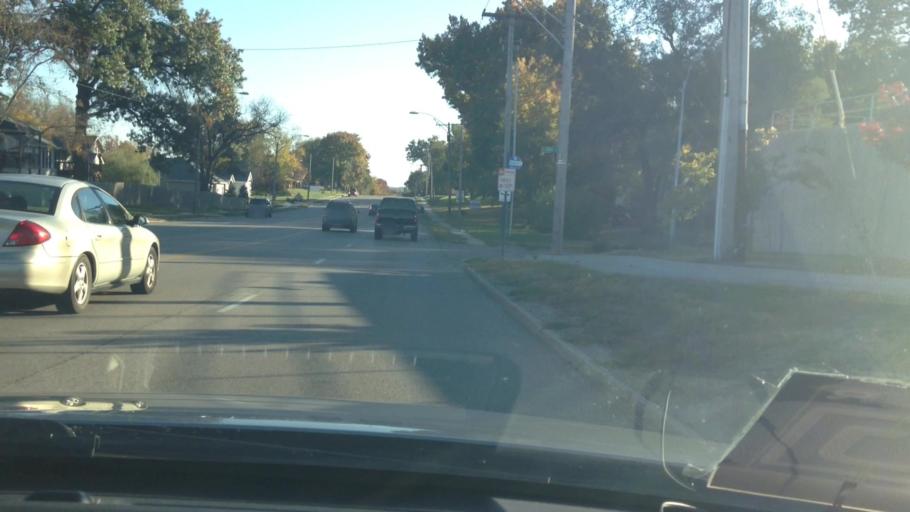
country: US
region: Missouri
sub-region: Clay County
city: Gladstone
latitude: 39.1846
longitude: -94.5490
